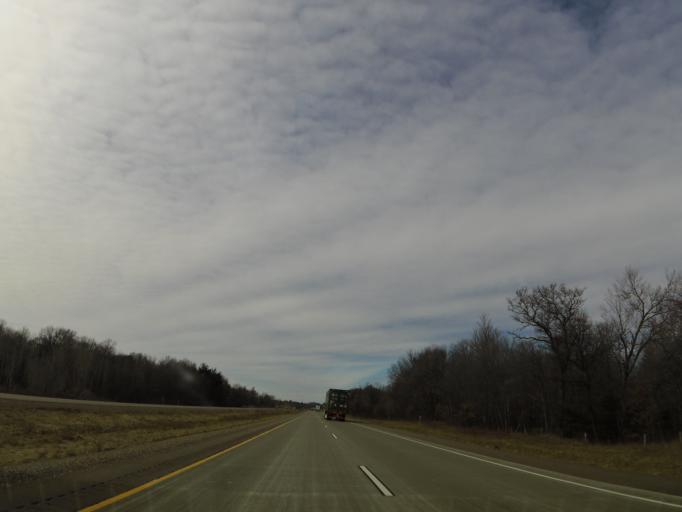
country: US
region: Wisconsin
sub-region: Jackson County
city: Black River Falls
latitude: 44.3565
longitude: -90.9544
